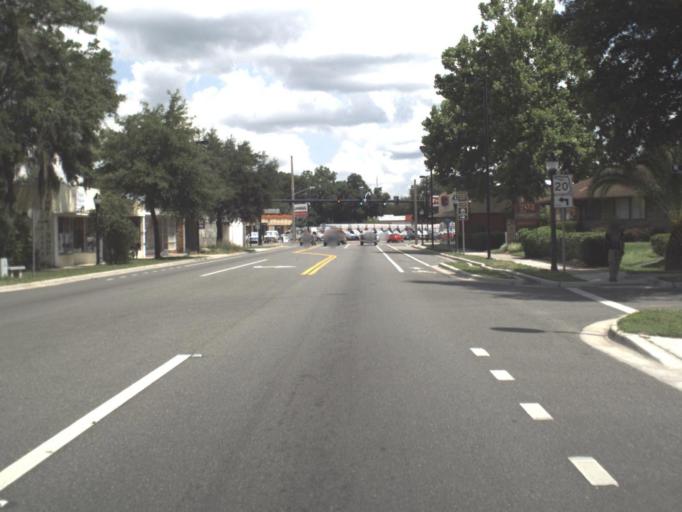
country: US
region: Florida
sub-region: Alachua County
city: Gainesville
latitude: 29.6578
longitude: -82.3250
